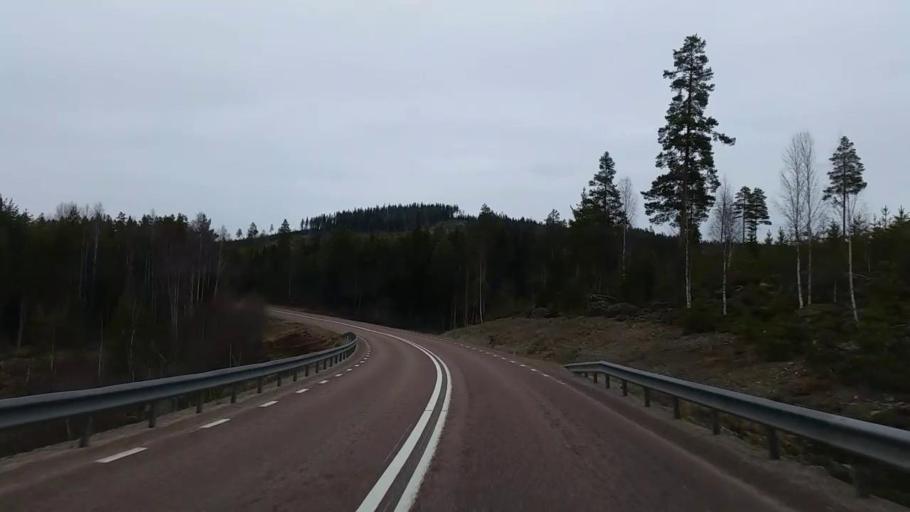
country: SE
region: Gaevleborg
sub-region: Ovanakers Kommun
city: Edsbyn
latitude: 61.2295
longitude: 15.8839
